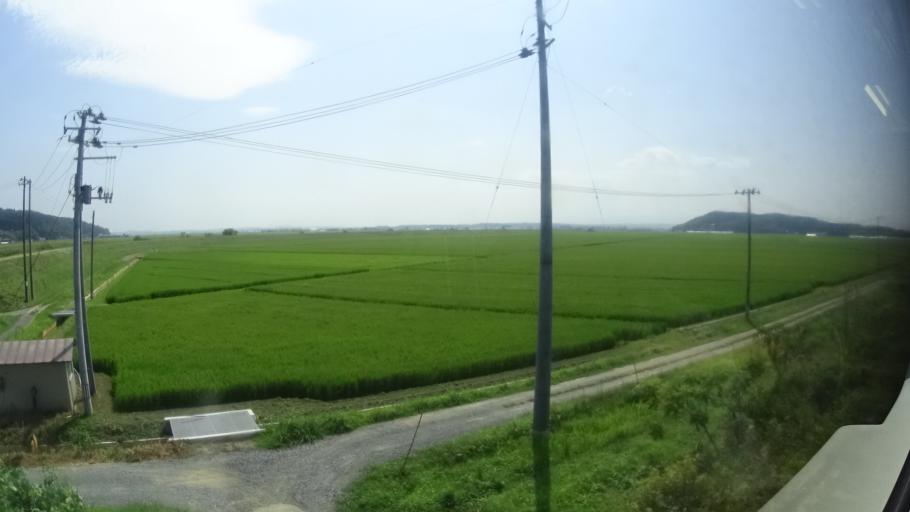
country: JP
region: Miyagi
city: Wakuya
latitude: 38.5192
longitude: 141.1733
